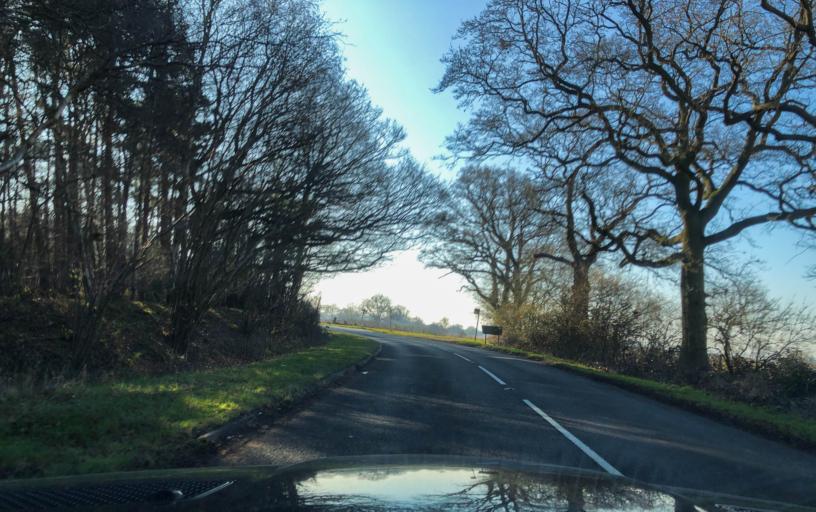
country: GB
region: England
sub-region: Warwickshire
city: Warwick
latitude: 52.2348
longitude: -1.5604
